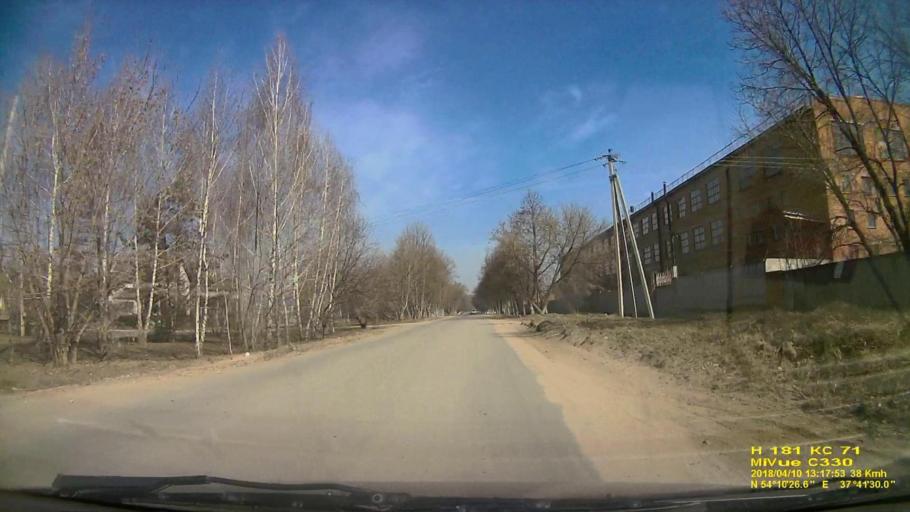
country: RU
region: Tula
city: Tula
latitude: 54.1741
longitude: 37.6917
